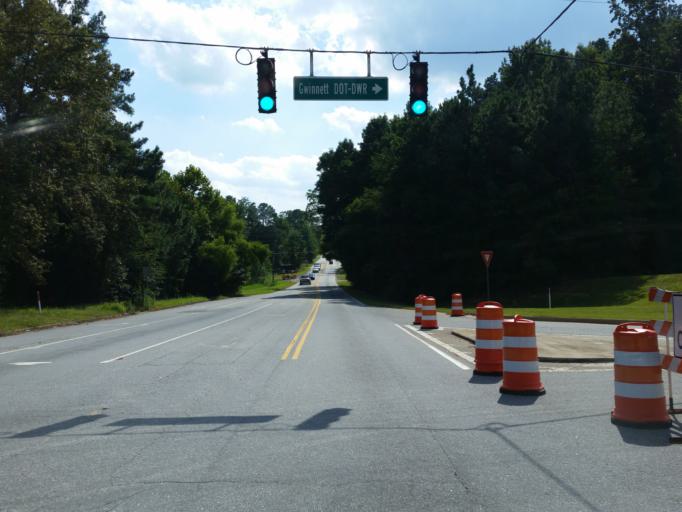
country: US
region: Georgia
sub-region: Gwinnett County
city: Lawrenceville
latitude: 33.9671
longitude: -83.9617
